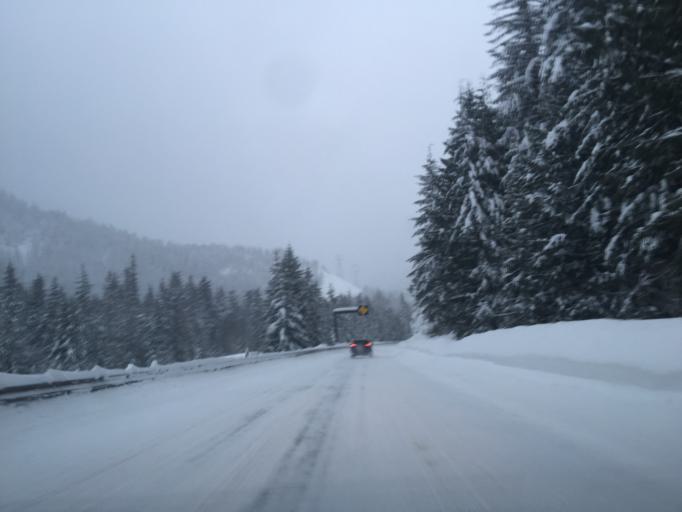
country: US
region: Washington
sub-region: Chelan County
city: Leavenworth
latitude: 47.7728
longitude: -121.0059
